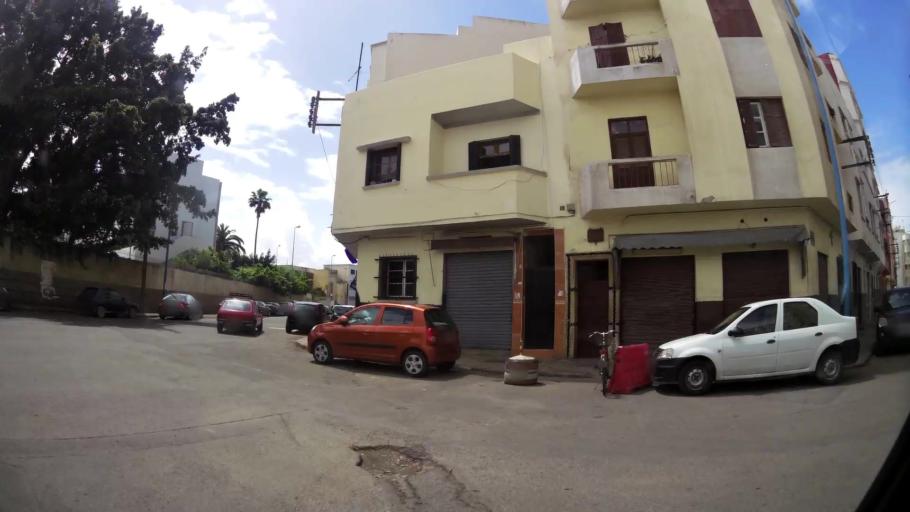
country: MA
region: Grand Casablanca
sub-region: Casablanca
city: Casablanca
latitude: 33.5970
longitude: -7.6359
